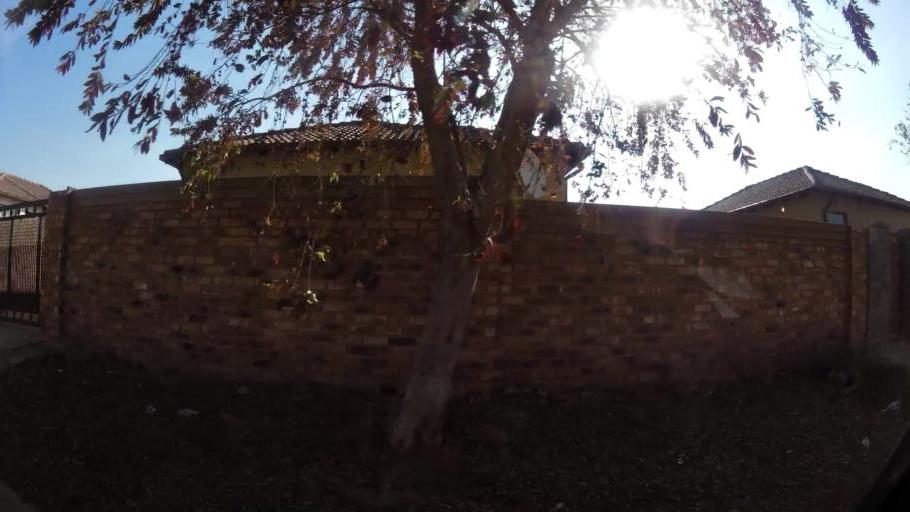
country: ZA
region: Gauteng
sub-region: West Rand District Municipality
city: Muldersdriseloop
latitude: -26.0393
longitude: 27.9130
